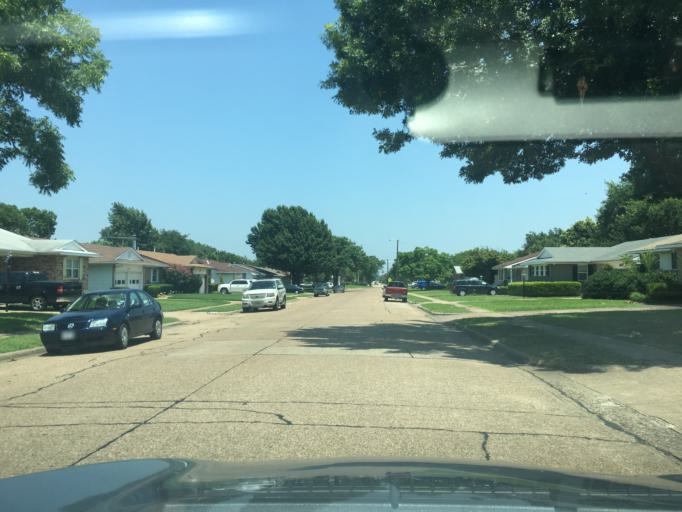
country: US
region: Texas
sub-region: Dallas County
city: Richardson
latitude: 32.9241
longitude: -96.7031
